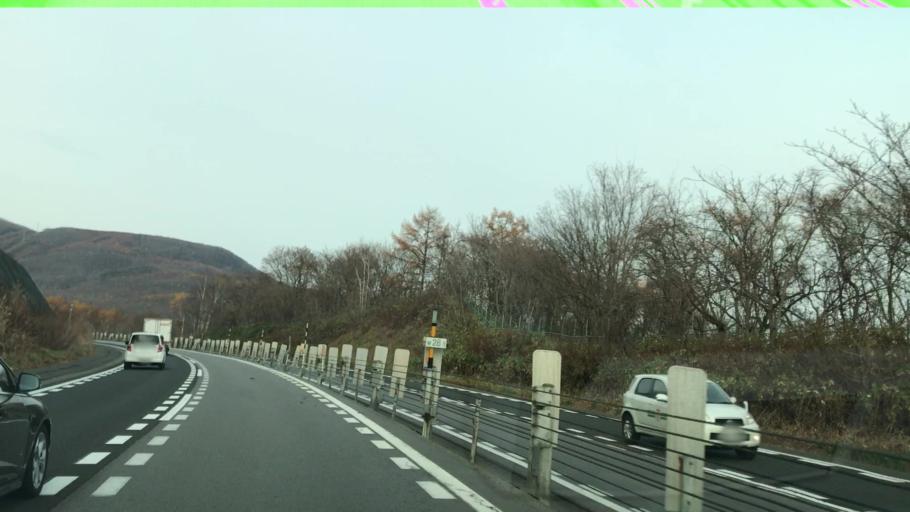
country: JP
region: Hokkaido
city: Otaru
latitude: 43.1517
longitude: 141.1257
